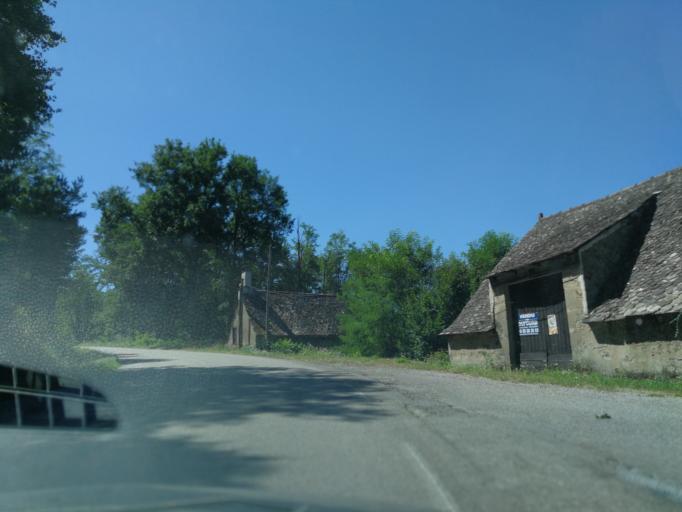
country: FR
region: Limousin
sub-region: Departement de la Correze
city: Argentat
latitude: 45.0770
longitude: 1.9447
